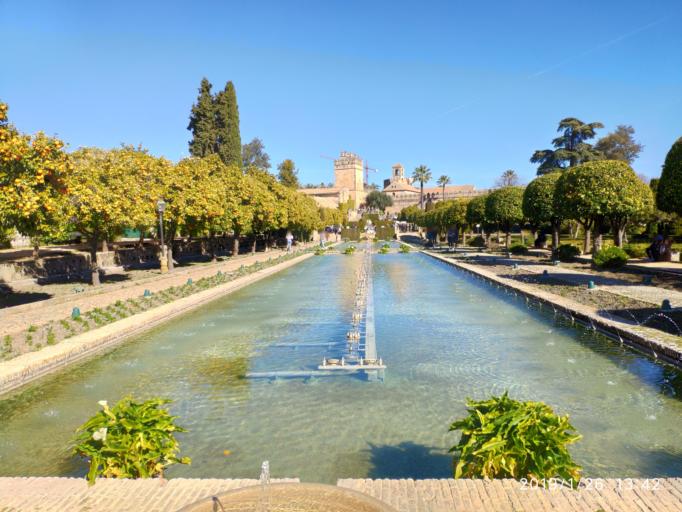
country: ES
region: Andalusia
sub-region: Province of Cordoba
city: Cordoba
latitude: 37.8755
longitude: -4.7831
